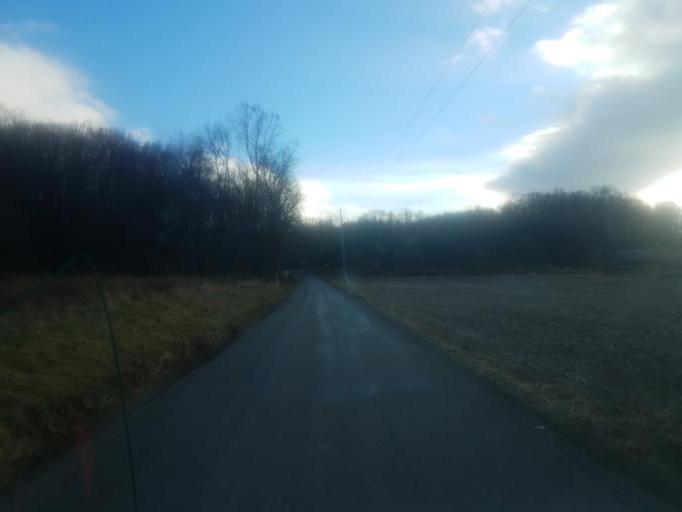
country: US
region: Ohio
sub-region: Sandusky County
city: Bellville
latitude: 40.6284
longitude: -82.3795
